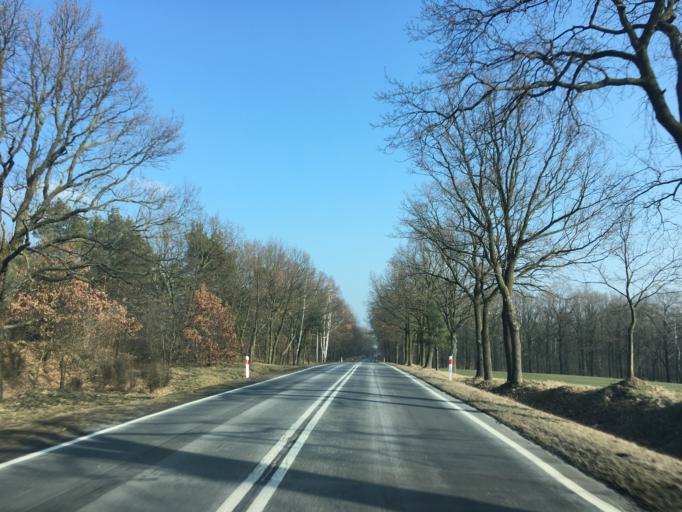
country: PL
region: Lower Silesian Voivodeship
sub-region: Powiat legnicki
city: Chojnow
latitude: 51.2764
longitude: 15.8510
